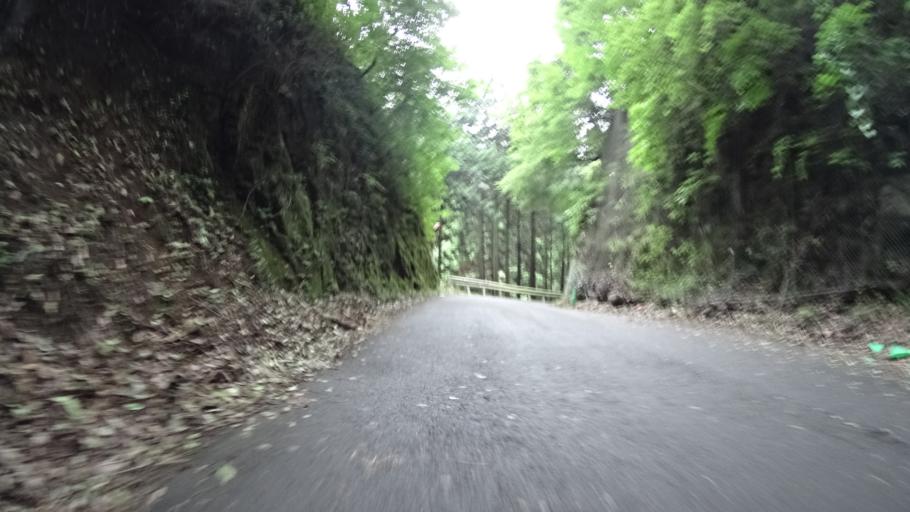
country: JP
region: Kanagawa
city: Hadano
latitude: 35.4989
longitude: 139.2267
